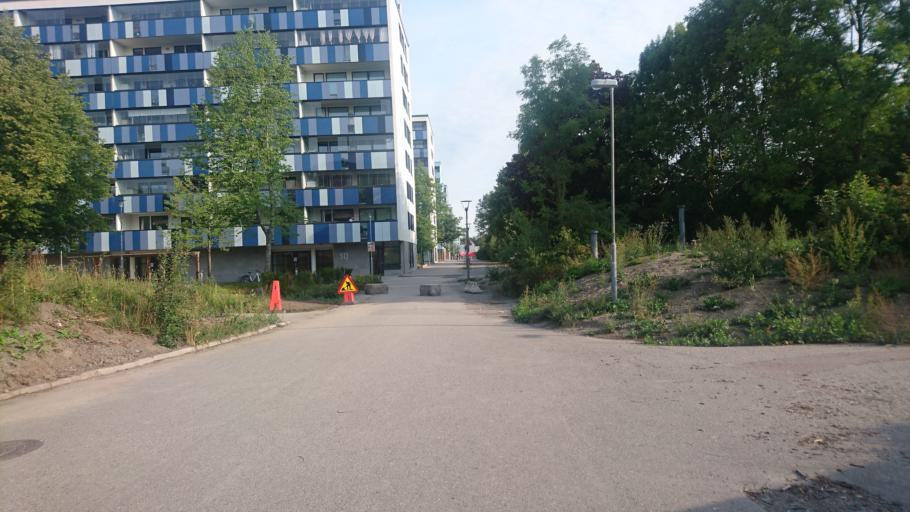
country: SE
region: Stockholm
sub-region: Upplands Vasby Kommun
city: Upplands Vaesby
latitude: 59.5144
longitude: 17.9115
